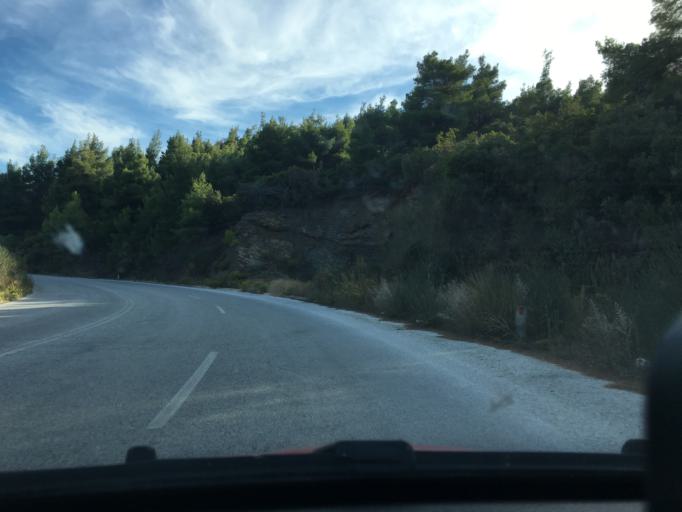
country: GR
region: Central Macedonia
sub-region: Nomos Chalkidikis
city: Agios Nikolaos
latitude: 40.2842
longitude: 23.6825
